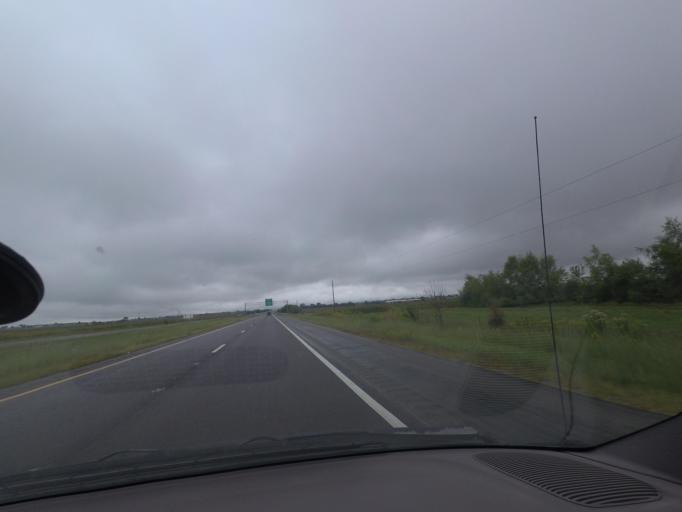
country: US
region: Illinois
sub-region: Champaign County
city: Champaign
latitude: 40.1204
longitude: -88.3316
